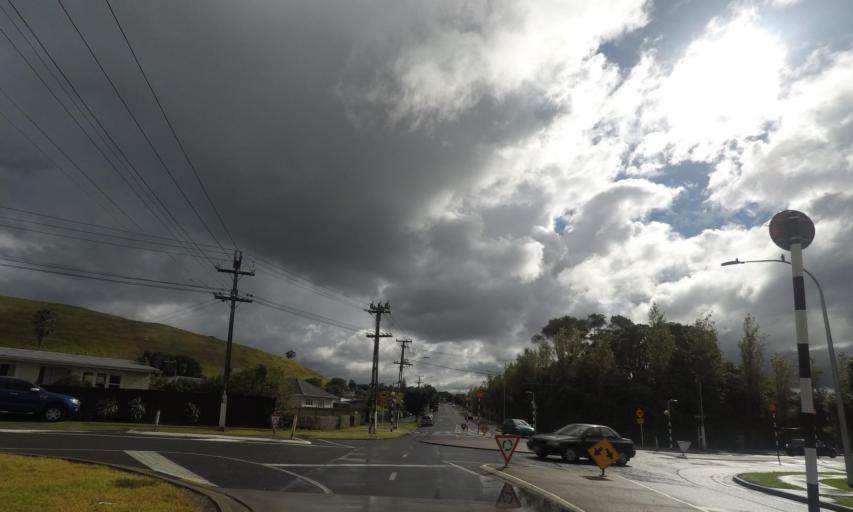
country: NZ
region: Auckland
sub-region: Auckland
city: Mangere
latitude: -36.9555
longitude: 174.7849
